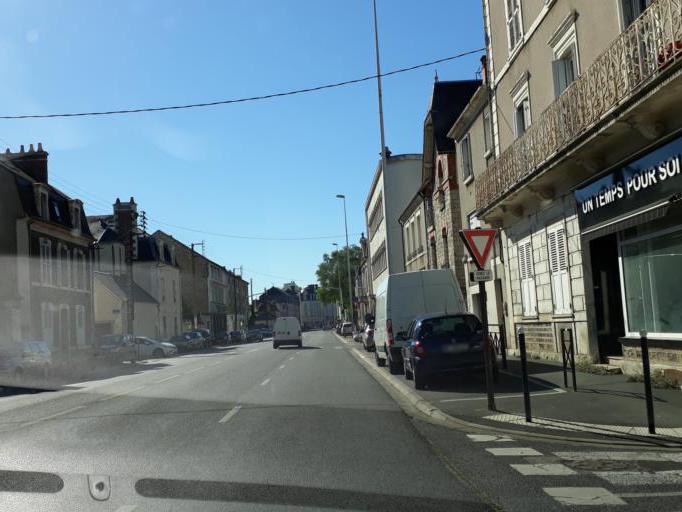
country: FR
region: Centre
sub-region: Departement du Cher
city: Bourges
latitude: 47.0851
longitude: 2.4021
